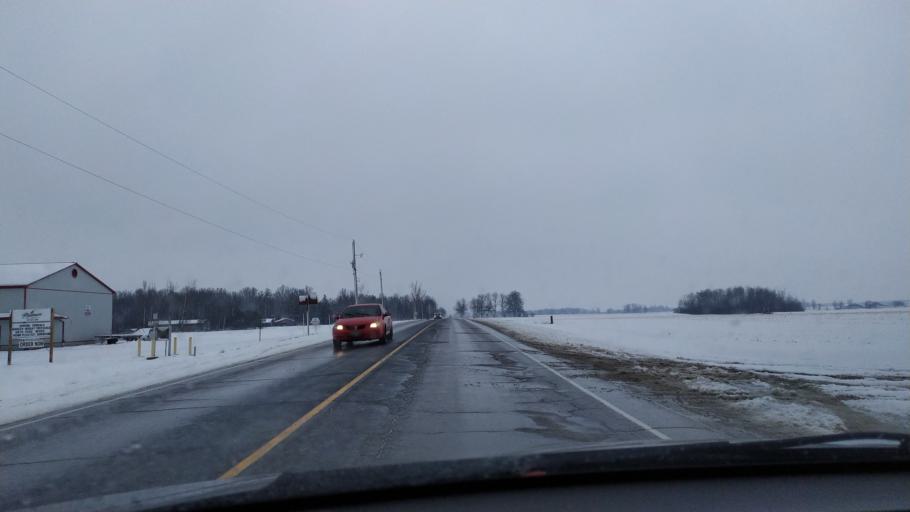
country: CA
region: Ontario
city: North Perth
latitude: 43.5763
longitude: -80.8362
